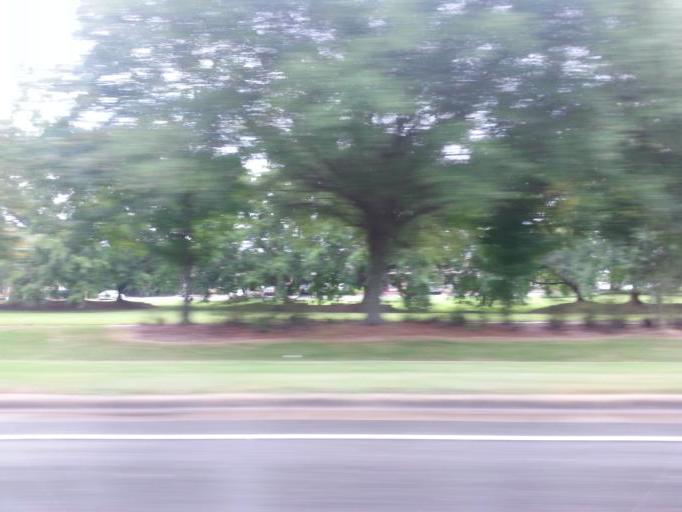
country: US
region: Alabama
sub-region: Baldwin County
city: Fairhope
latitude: 30.5250
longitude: -87.8861
